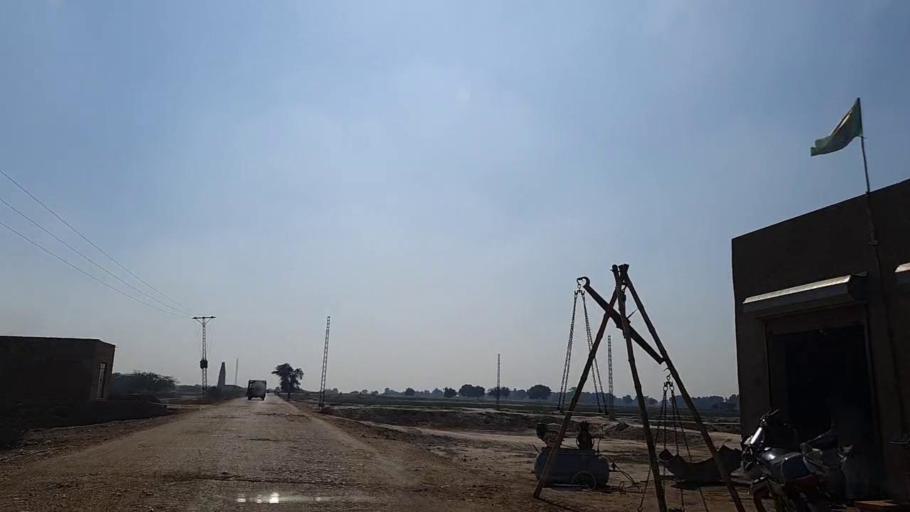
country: PK
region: Sindh
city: Sakrand
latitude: 26.2936
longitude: 68.1081
